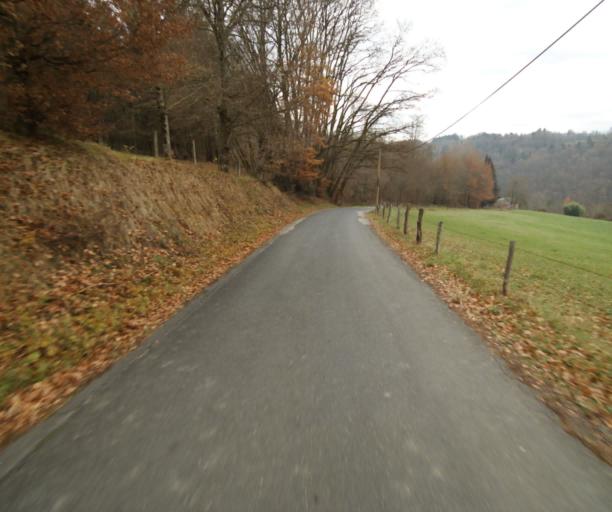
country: FR
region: Limousin
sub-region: Departement de la Correze
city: Tulle
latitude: 45.2448
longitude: 1.7378
